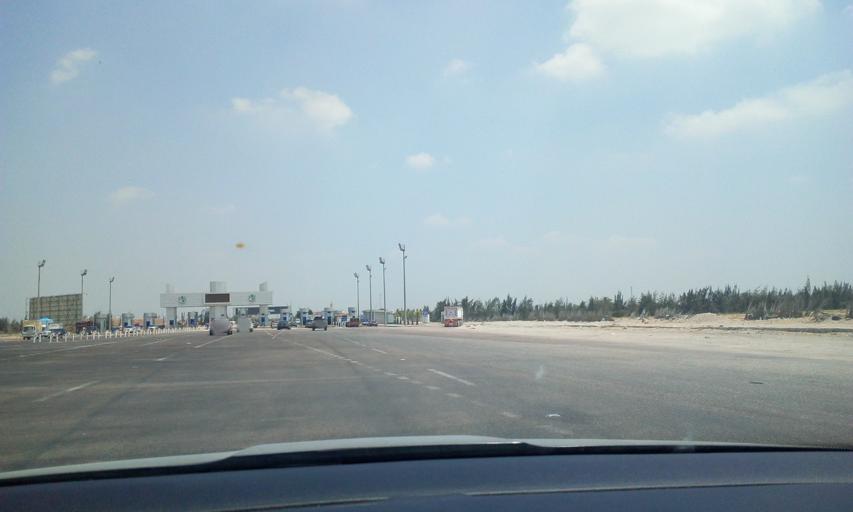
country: EG
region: Al Buhayrah
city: Beheira
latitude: 30.5117
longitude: 30.2203
